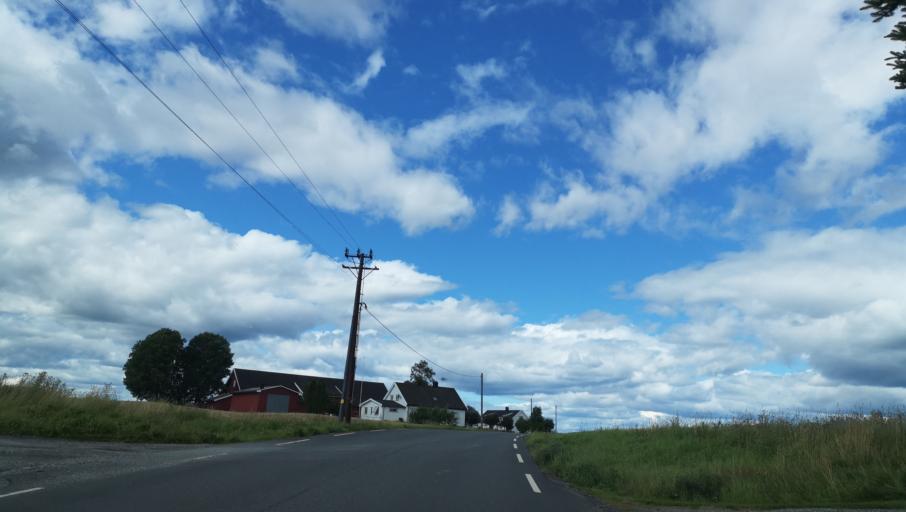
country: NO
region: Akershus
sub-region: Ski
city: Ski
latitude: 59.6973
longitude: 10.8958
